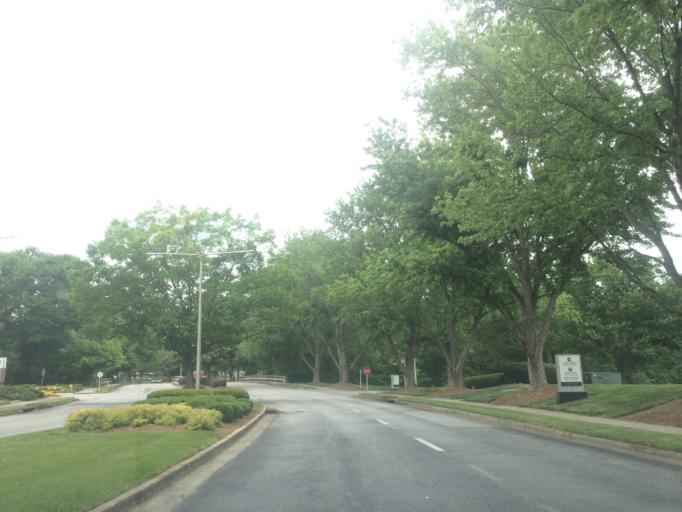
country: US
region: Georgia
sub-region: DeKalb County
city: North Druid Hills
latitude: 33.8451
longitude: -84.3070
